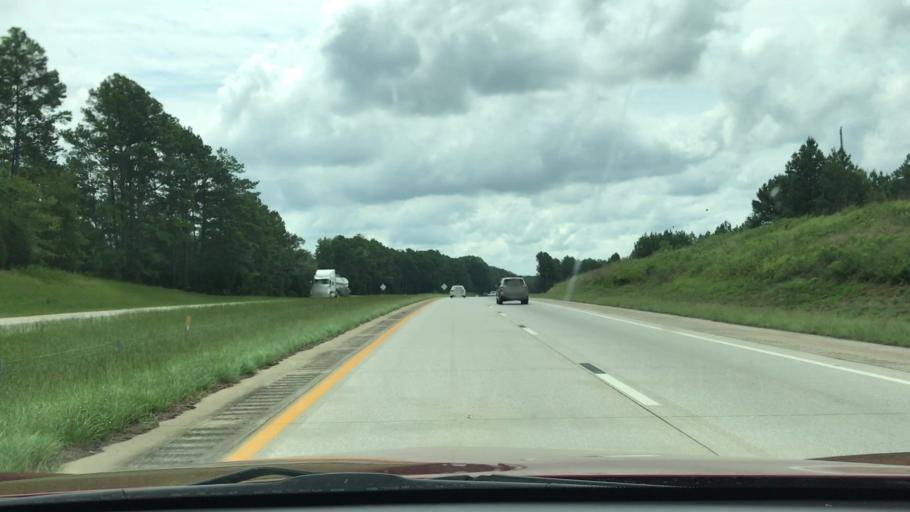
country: US
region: South Carolina
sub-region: Laurens County
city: Laurens
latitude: 34.6068
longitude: -82.0679
